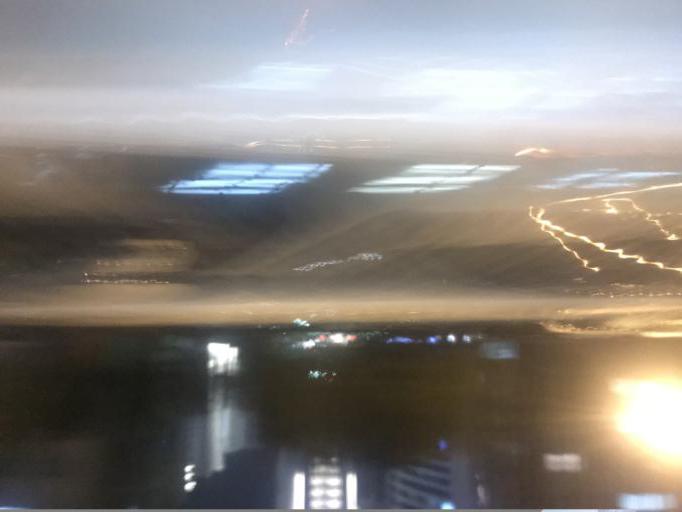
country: TR
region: Istanbul
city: Bahcelievler
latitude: 40.9777
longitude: 28.8571
